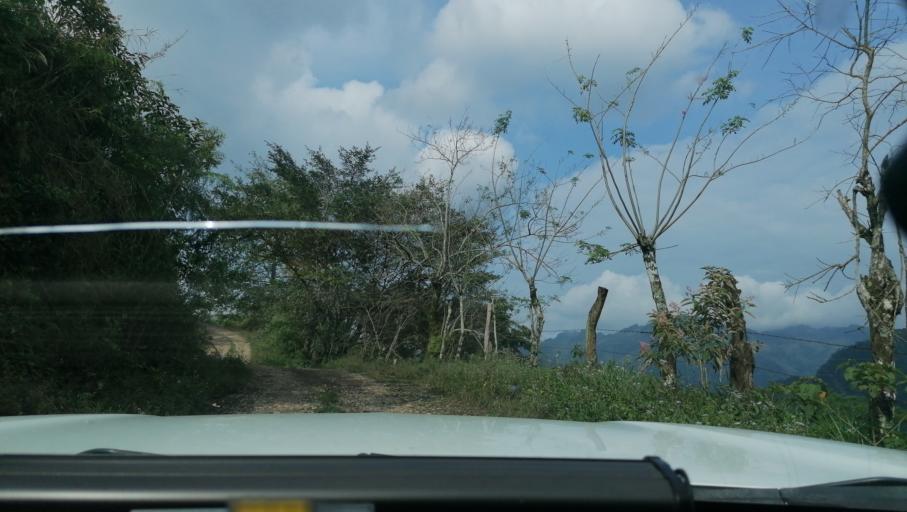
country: MX
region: Chiapas
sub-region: Tapilula
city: San Francisco Jacona
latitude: 17.3028
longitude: -93.1032
